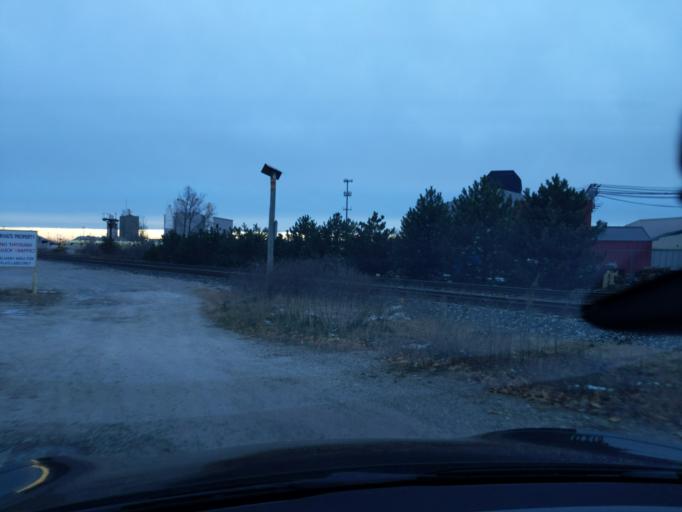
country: US
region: Michigan
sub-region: Ingham County
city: Lansing
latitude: 42.7518
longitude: -84.5466
